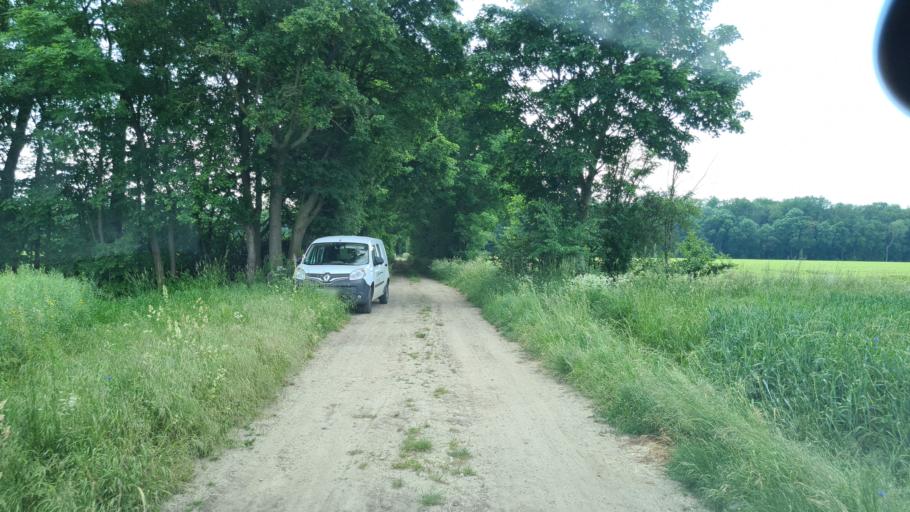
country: DE
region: Brandenburg
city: Sonnewalde
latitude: 51.7064
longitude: 13.6363
